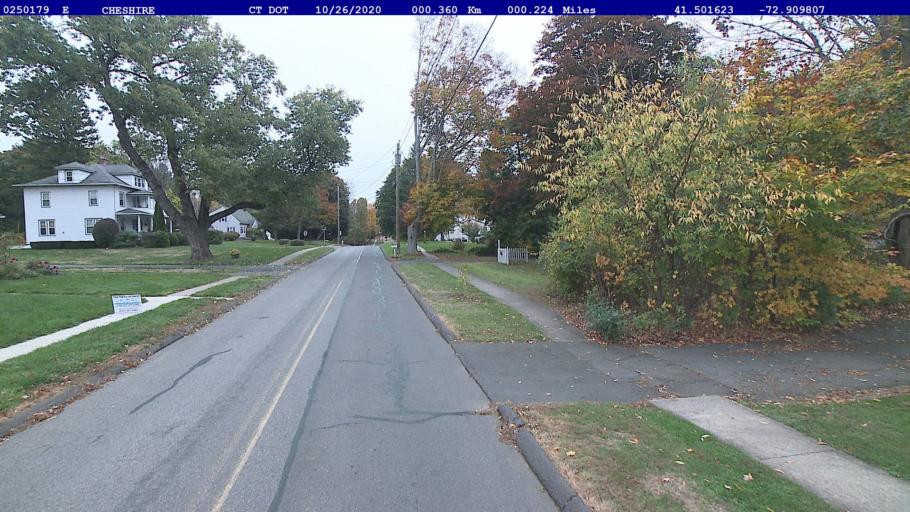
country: US
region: Connecticut
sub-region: New Haven County
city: Cheshire
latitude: 41.5016
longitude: -72.9098
